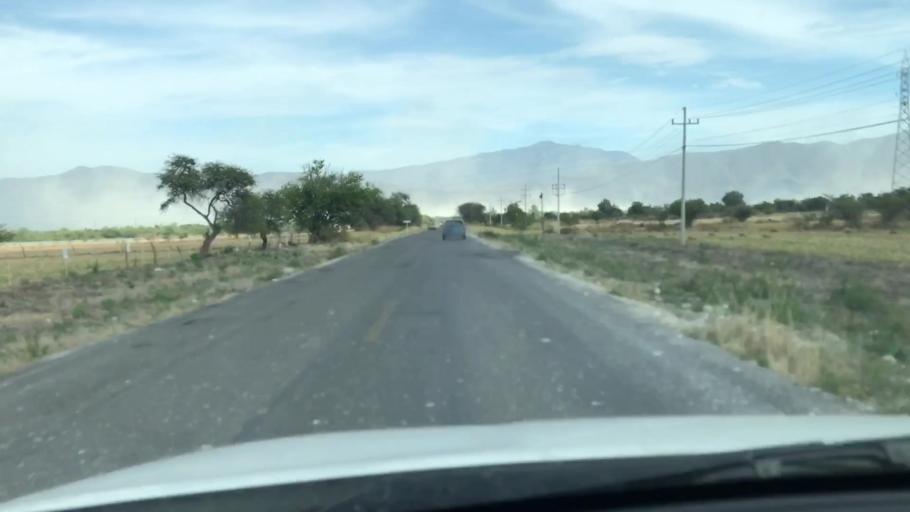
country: MX
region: Jalisco
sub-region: Zacoalco de Torres
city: Barranca de Otates (Barranca de Otatan)
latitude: 20.2858
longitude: -103.6131
